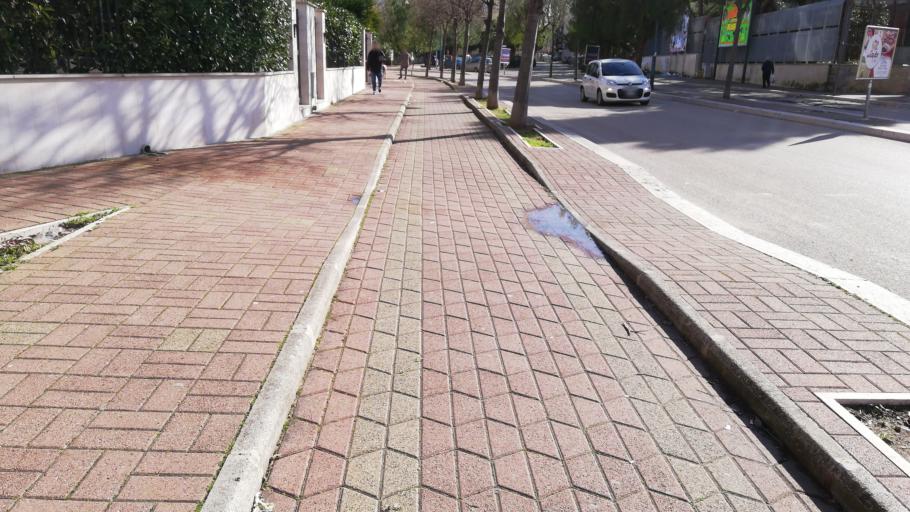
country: IT
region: Apulia
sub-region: Provincia di Barletta - Andria - Trani
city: Andria
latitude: 41.2335
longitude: 16.3019
